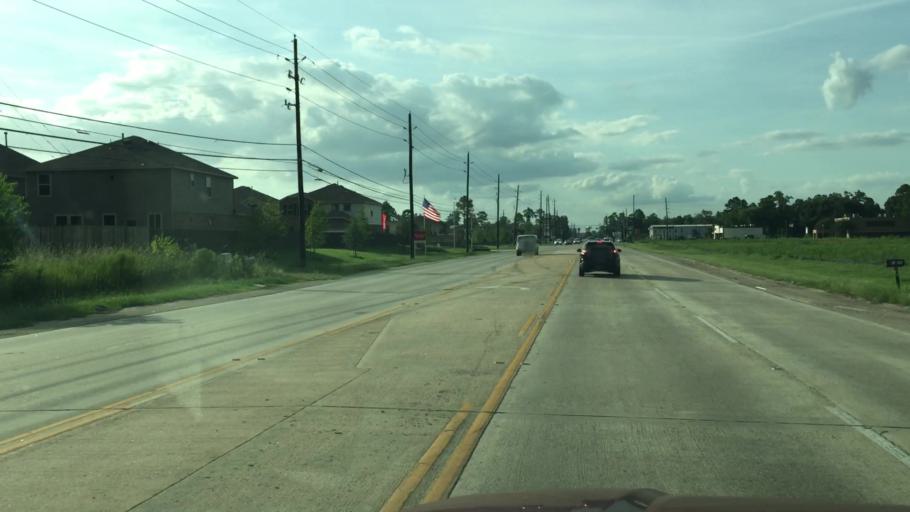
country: US
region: Texas
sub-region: Harris County
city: Hudson
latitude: 29.9962
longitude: -95.5044
